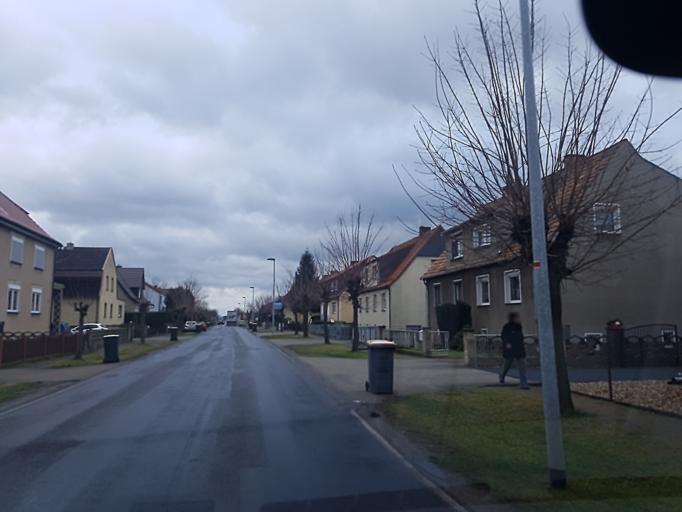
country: DE
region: Brandenburg
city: Bad Liebenwerda
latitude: 51.5091
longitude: 13.3916
